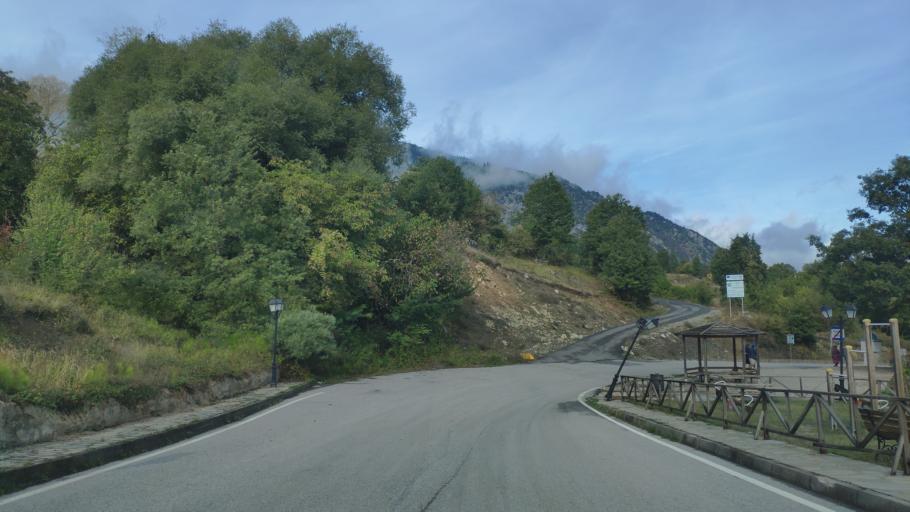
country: GR
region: West Macedonia
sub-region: Nomos Kastorias
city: Nestorio
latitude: 40.2761
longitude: 20.9744
